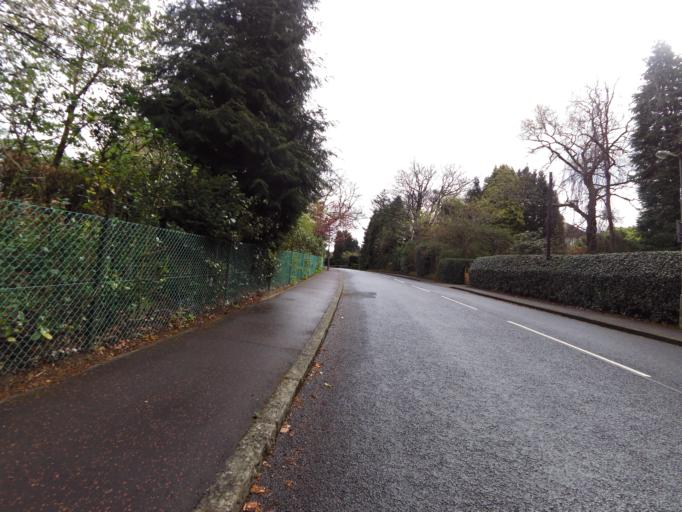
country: GB
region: Scotland
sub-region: Edinburgh
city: Colinton
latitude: 55.9658
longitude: -3.2913
